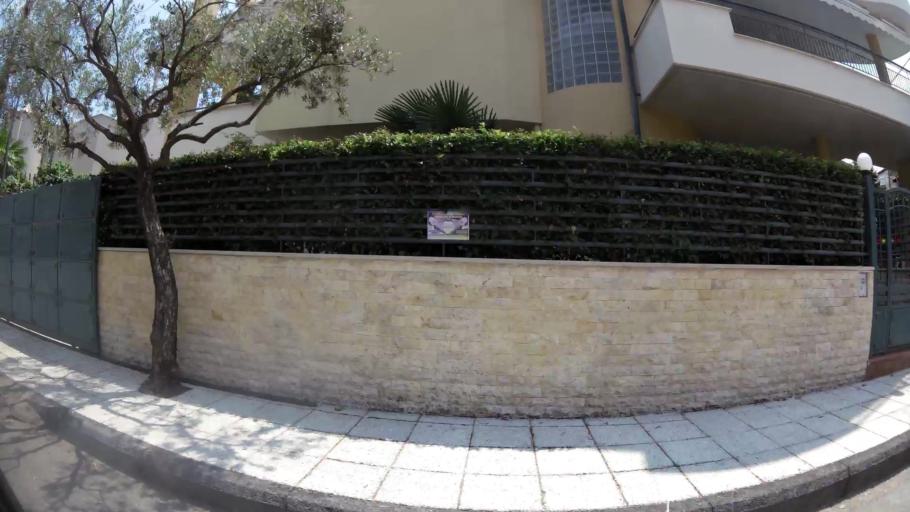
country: GR
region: Central Macedonia
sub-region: Nomos Imathias
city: Veroia
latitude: 40.5133
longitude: 22.1818
